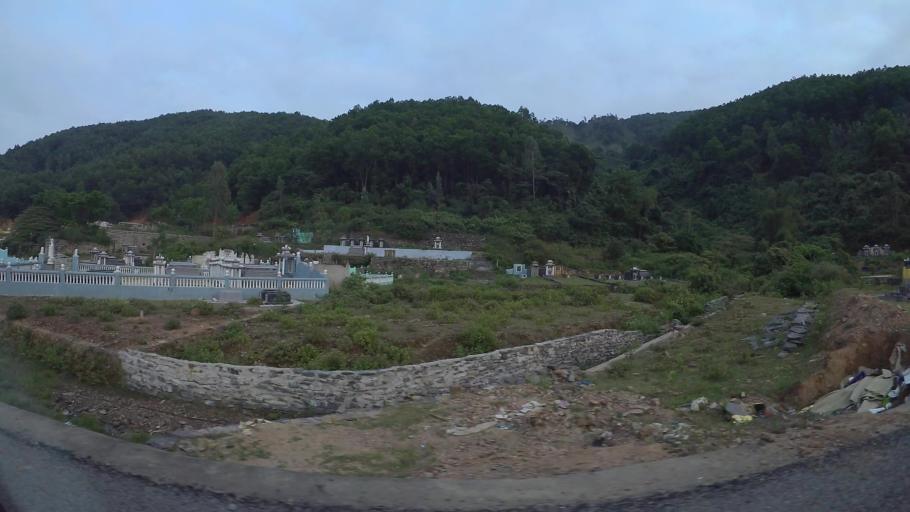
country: VN
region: Da Nang
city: Lien Chieu
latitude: 16.0558
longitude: 108.1259
